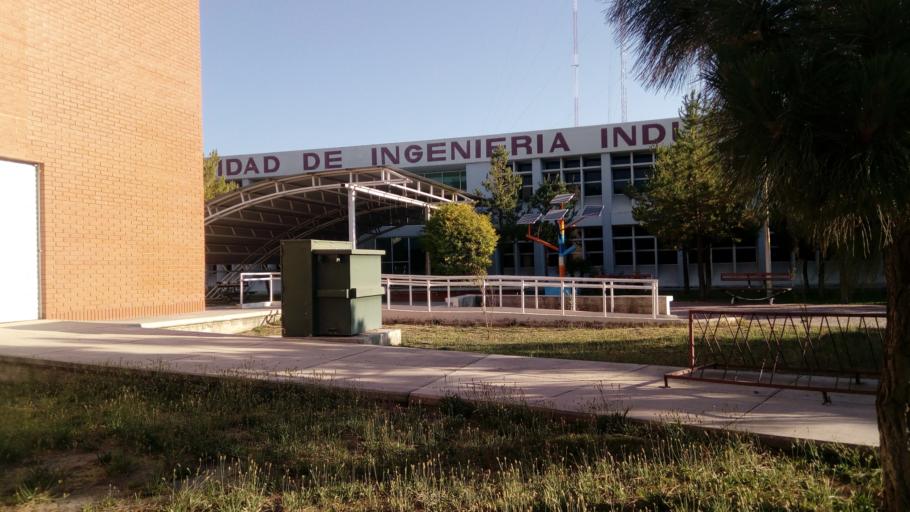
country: MX
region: Durango
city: Victoria de Durango
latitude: 24.0346
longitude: -104.6452
